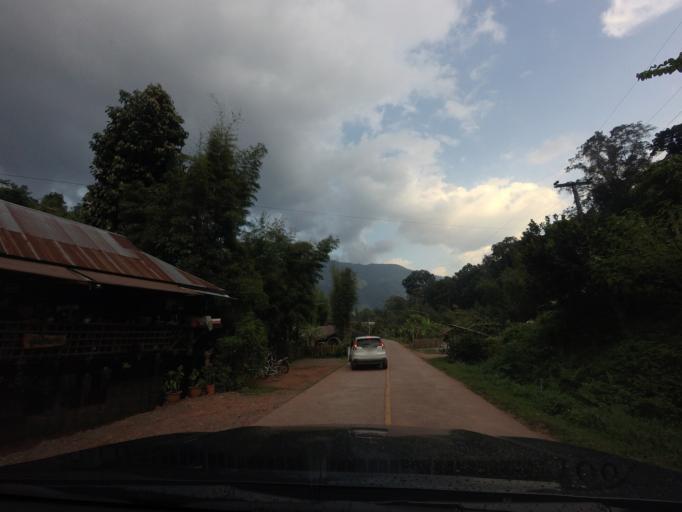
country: TH
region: Nan
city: Bo Kluea
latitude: 19.1927
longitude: 101.1967
